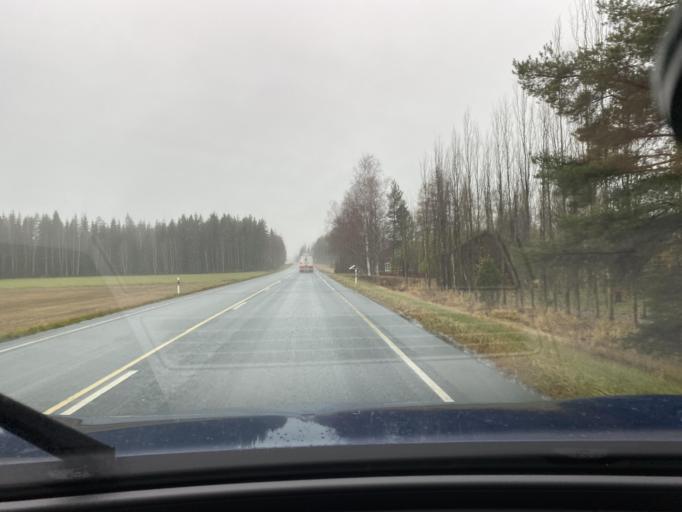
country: FI
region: Haeme
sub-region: Forssa
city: Jokioinen
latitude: 60.7801
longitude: 23.4139
